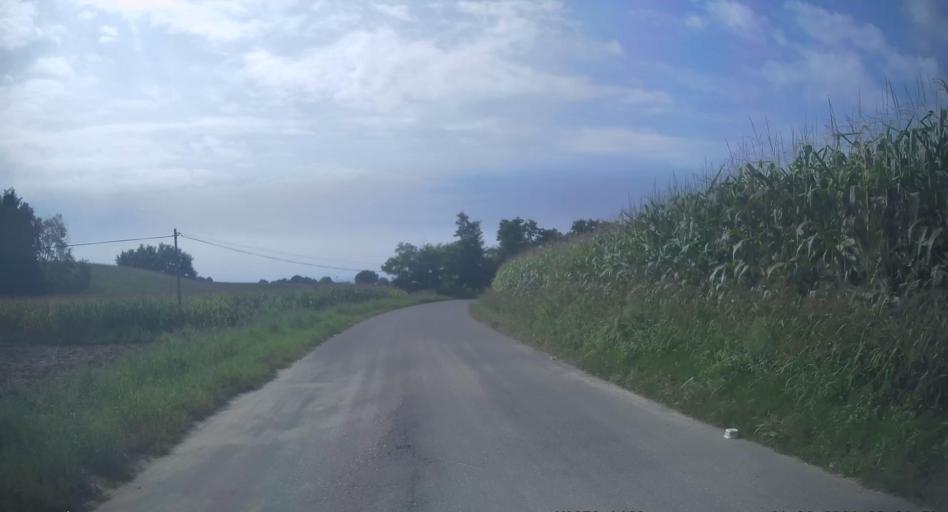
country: PL
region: Lesser Poland Voivodeship
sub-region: Powiat proszowicki
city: Nowe Brzesko
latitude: 50.1532
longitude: 20.4411
